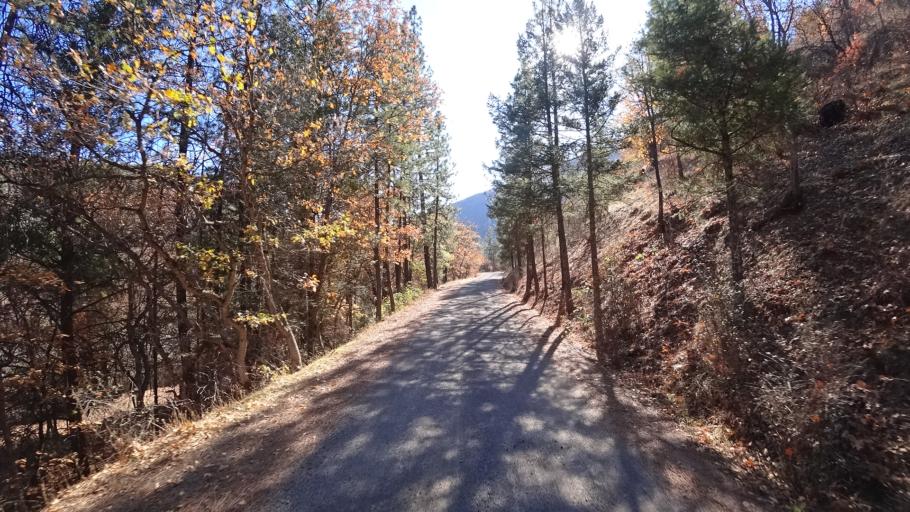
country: US
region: California
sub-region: Siskiyou County
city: Yreka
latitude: 41.8600
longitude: -122.7062
